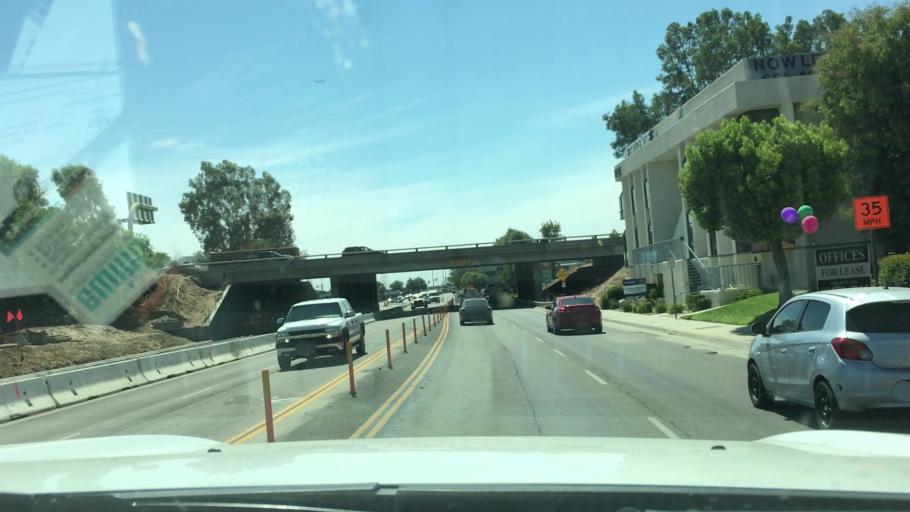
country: US
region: California
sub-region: Kern County
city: Bakersfield
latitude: 35.3739
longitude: -119.0429
